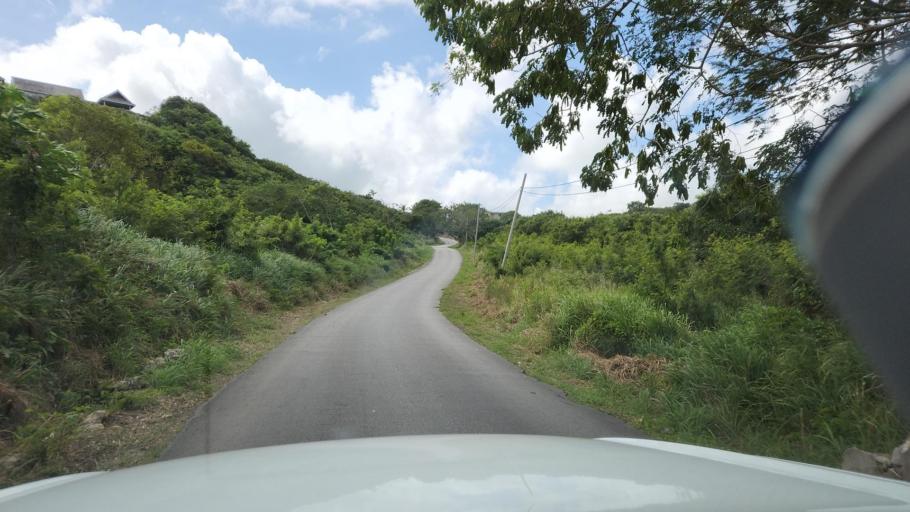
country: BB
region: Saint John
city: Four Cross Roads
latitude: 13.1629
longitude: -59.4741
